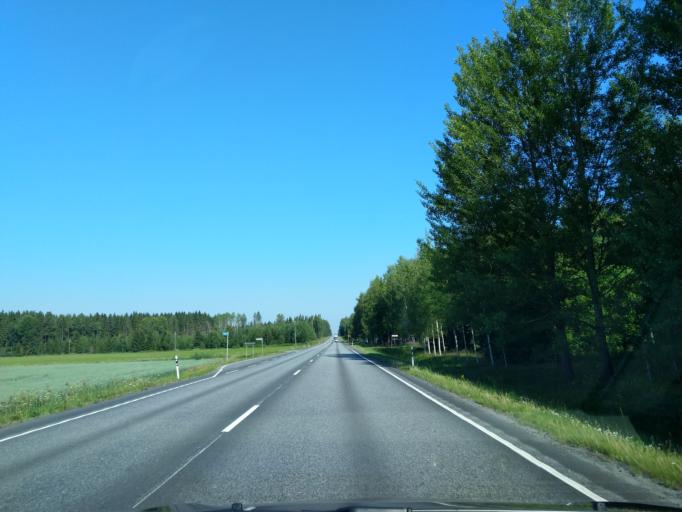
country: FI
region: Varsinais-Suomi
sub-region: Loimaa
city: Alastaro
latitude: 61.0686
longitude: 22.9253
